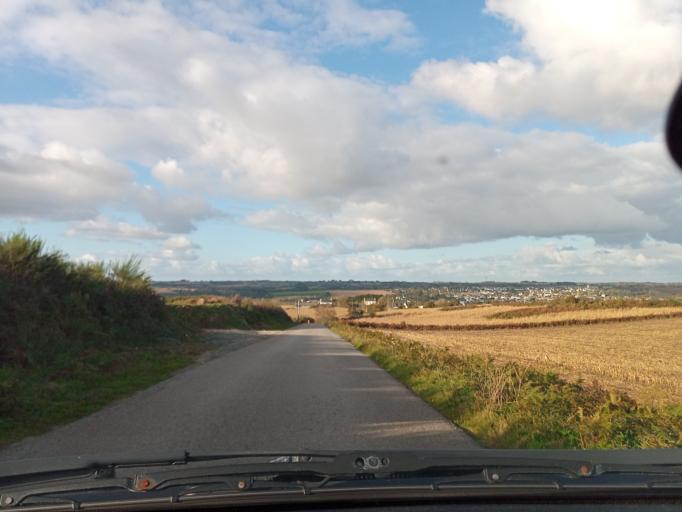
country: FR
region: Brittany
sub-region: Departement du Finistere
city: Plouhinec
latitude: 48.0264
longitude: -4.4982
